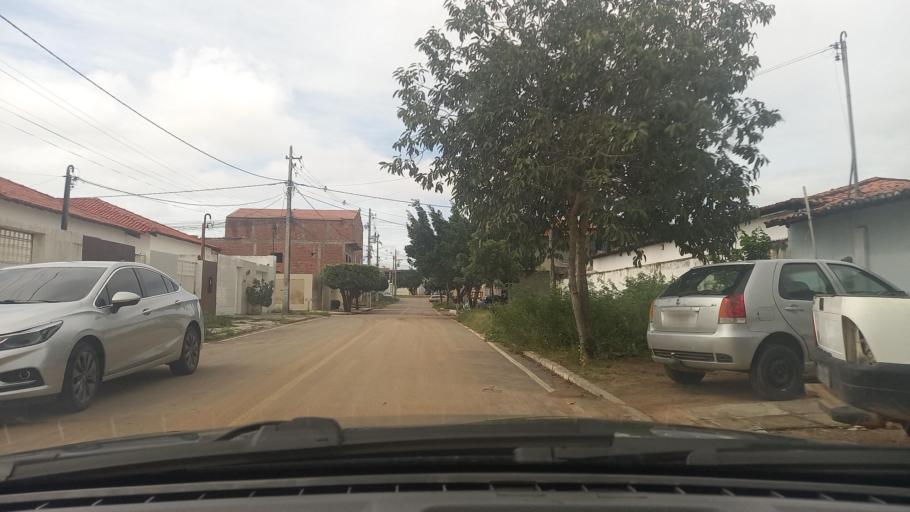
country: BR
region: Bahia
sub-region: Paulo Afonso
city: Paulo Afonso
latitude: -9.4041
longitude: -38.2399
